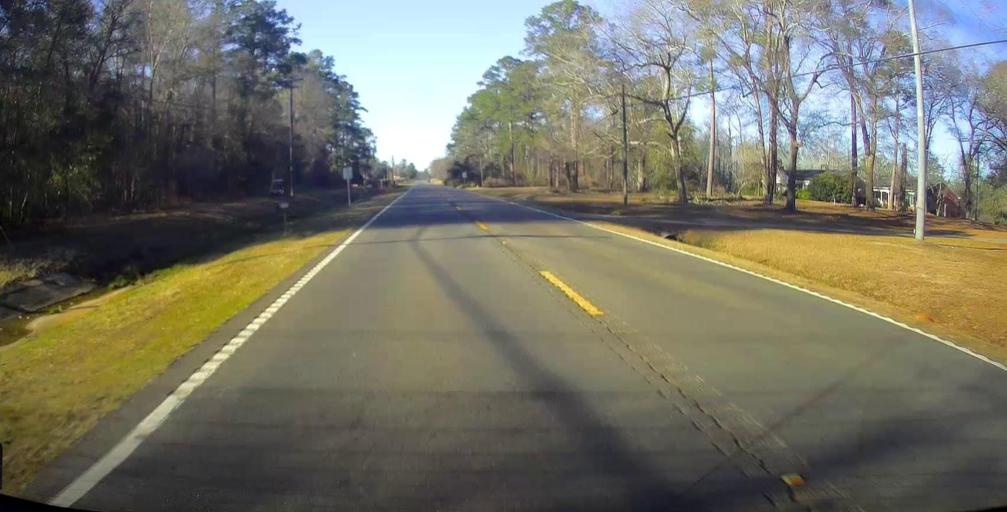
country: US
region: Georgia
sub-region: Sumter County
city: Americus
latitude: 32.0410
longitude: -84.2216
